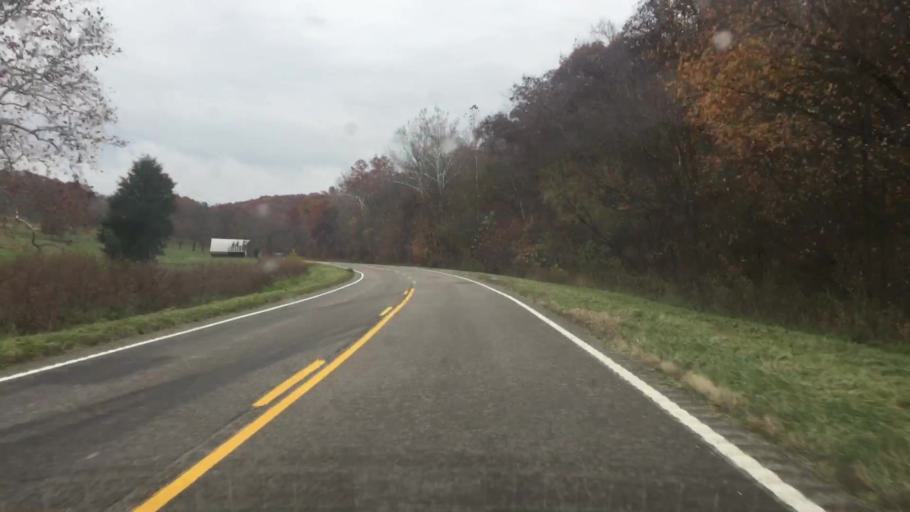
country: US
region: Missouri
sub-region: Gasconade County
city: Hermann
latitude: 38.7180
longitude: -91.6568
